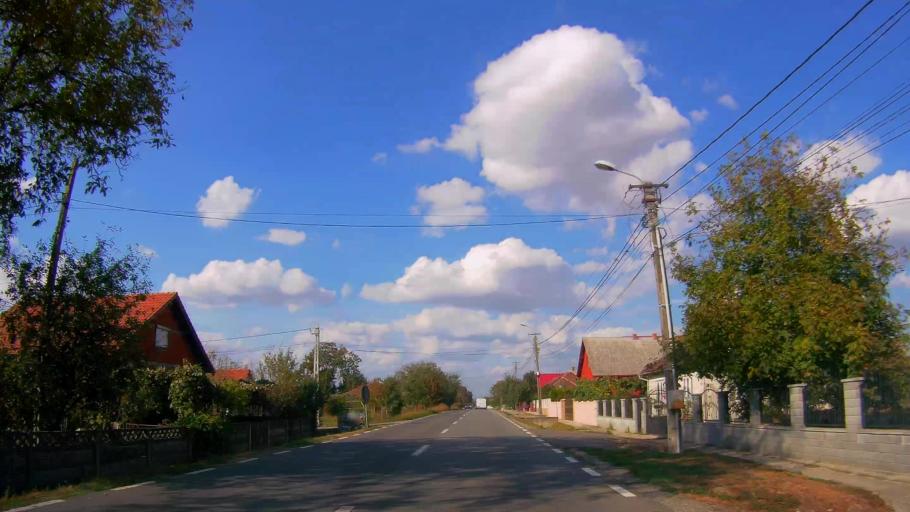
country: RO
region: Satu Mare
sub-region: Comuna Turulung
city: Draguseni
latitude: 47.8954
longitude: 23.0743
